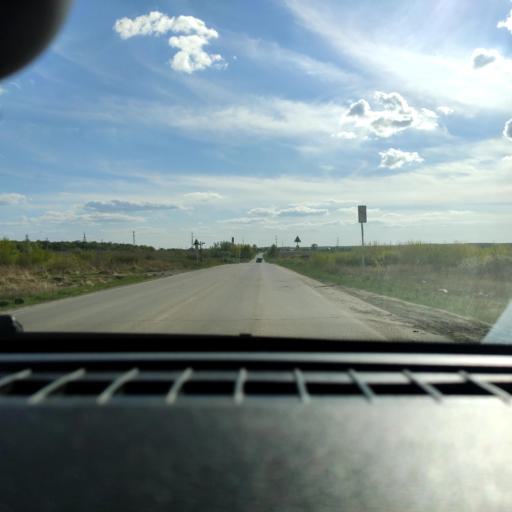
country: RU
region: Samara
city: Zhigulevsk
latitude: 53.3678
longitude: 49.4848
